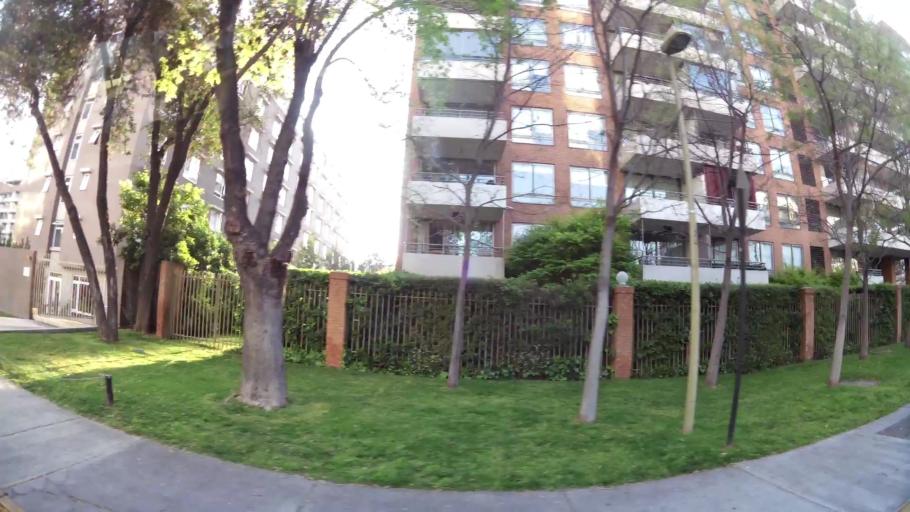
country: CL
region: Santiago Metropolitan
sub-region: Provincia de Santiago
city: Villa Presidente Frei, Nunoa, Santiago, Chile
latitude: -33.3998
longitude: -70.5550
